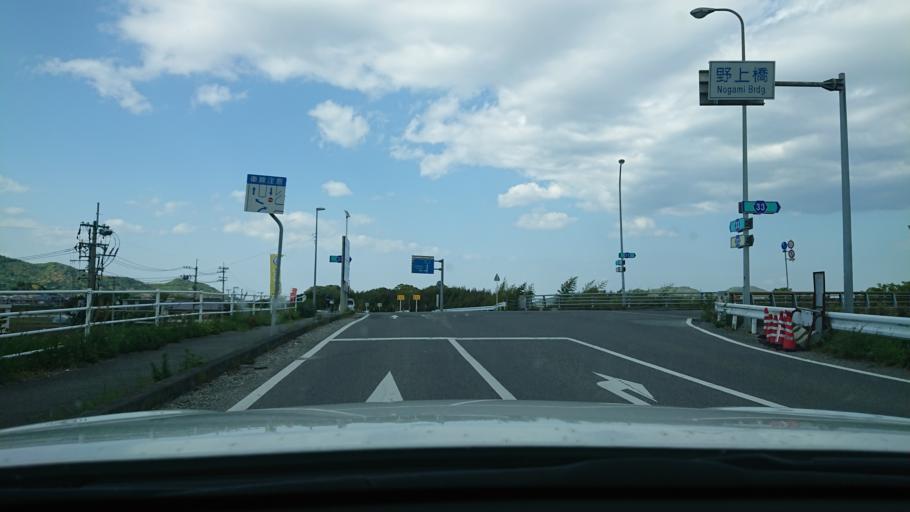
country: JP
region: Tokushima
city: Komatsushimacho
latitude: 33.9949
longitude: 134.5471
